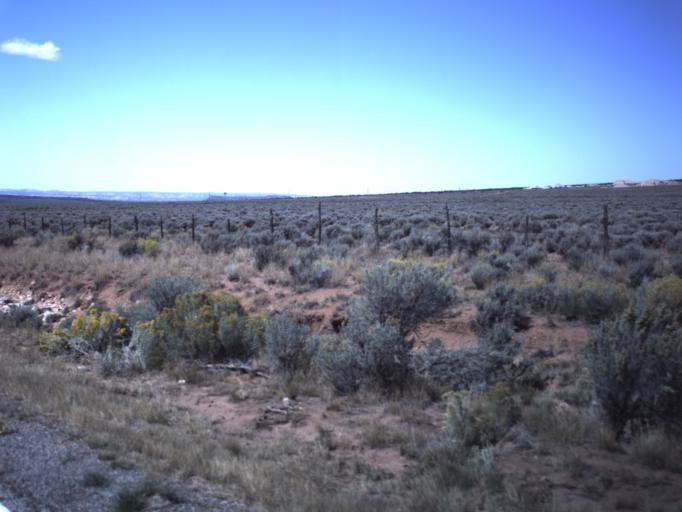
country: US
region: Utah
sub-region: Grand County
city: Moab
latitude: 38.3096
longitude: -109.2763
